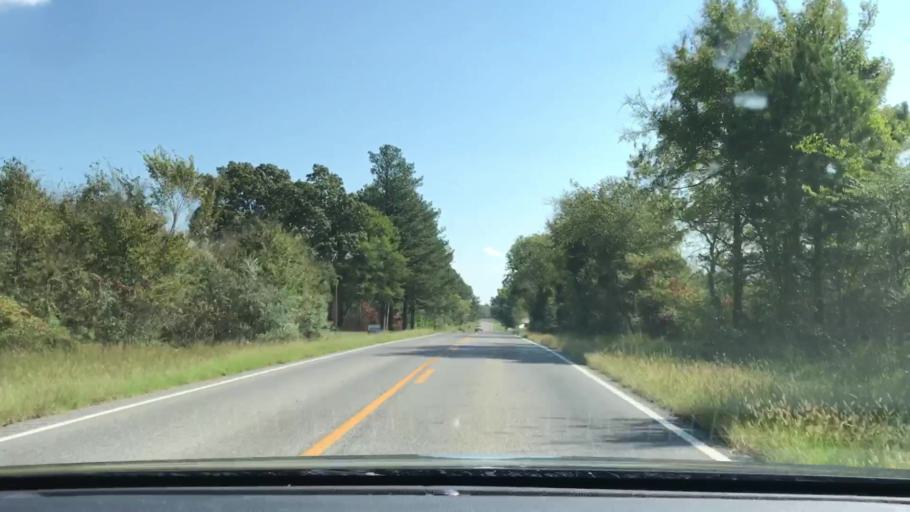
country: US
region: Kentucky
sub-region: Marshall County
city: Benton
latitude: 36.7639
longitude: -88.2050
